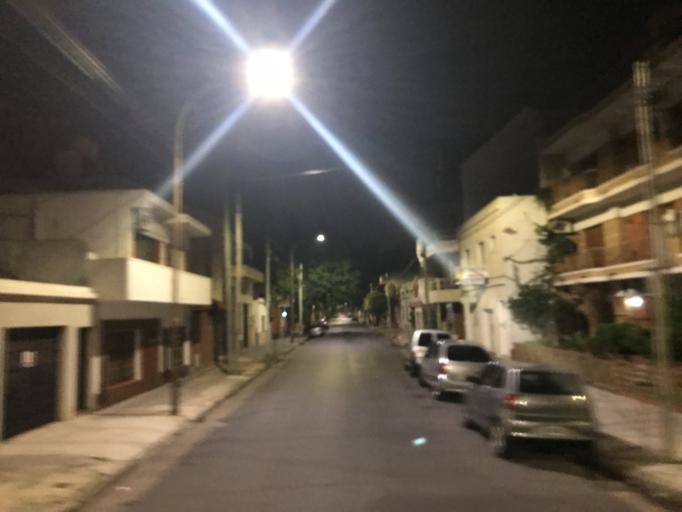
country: AR
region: Buenos Aires
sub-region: Partido de Lanus
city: Lanus
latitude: -34.6744
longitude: -58.4064
